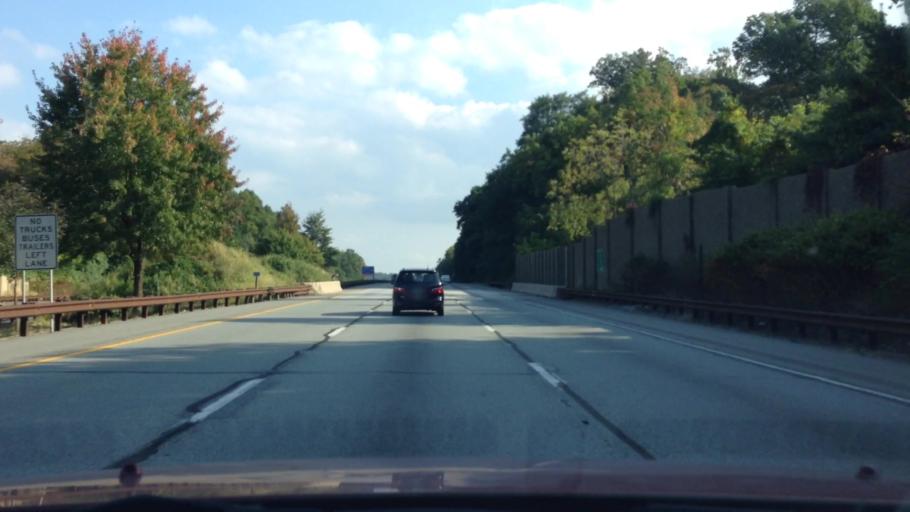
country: US
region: Pennsylvania
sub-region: Delaware County
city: Radnor
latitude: 40.0152
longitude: -75.3577
